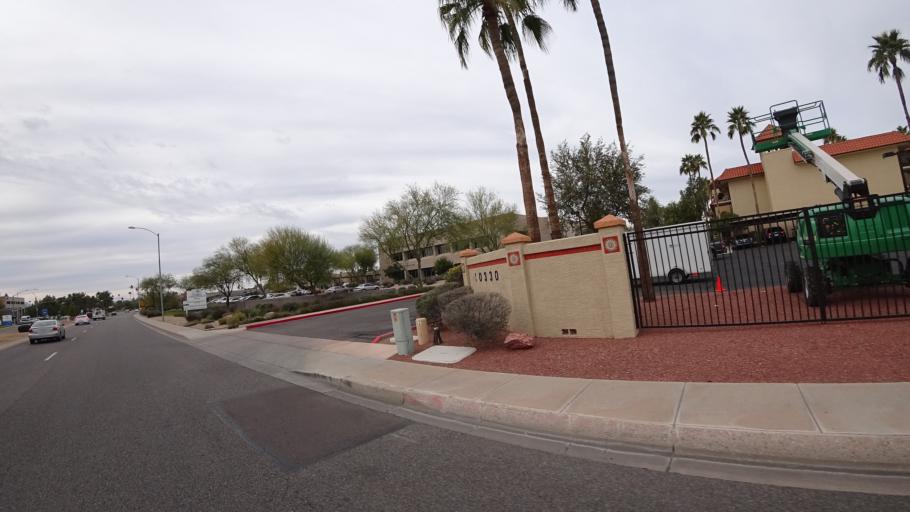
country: US
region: Arizona
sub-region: Maricopa County
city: Sun City
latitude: 33.6050
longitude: -112.2833
